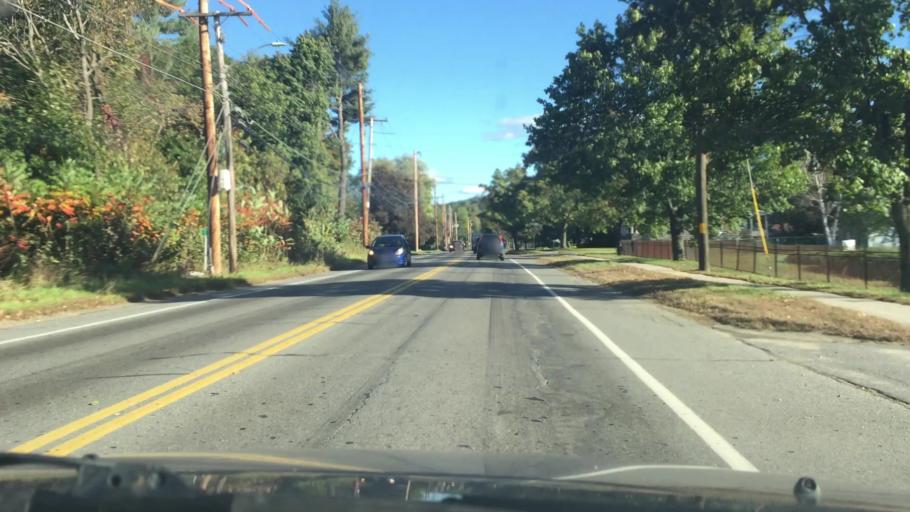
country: US
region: New Hampshire
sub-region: Cheshire County
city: Keene
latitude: 42.9154
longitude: -72.2708
